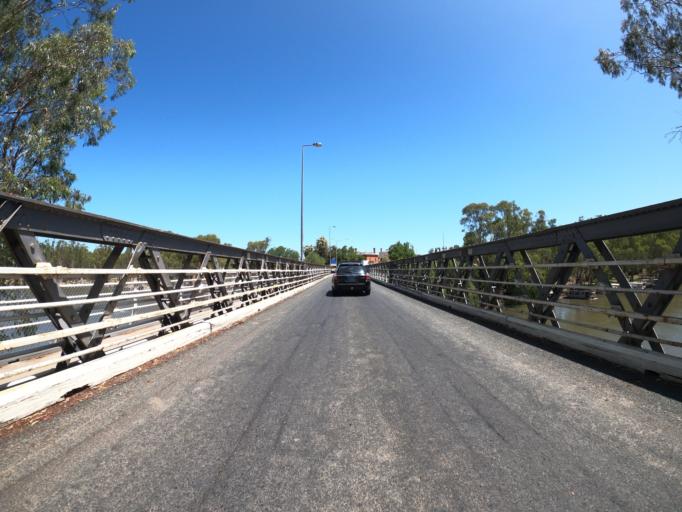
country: AU
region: New South Wales
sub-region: Corowa Shire
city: Corowa
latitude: -36.0064
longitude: 146.3954
